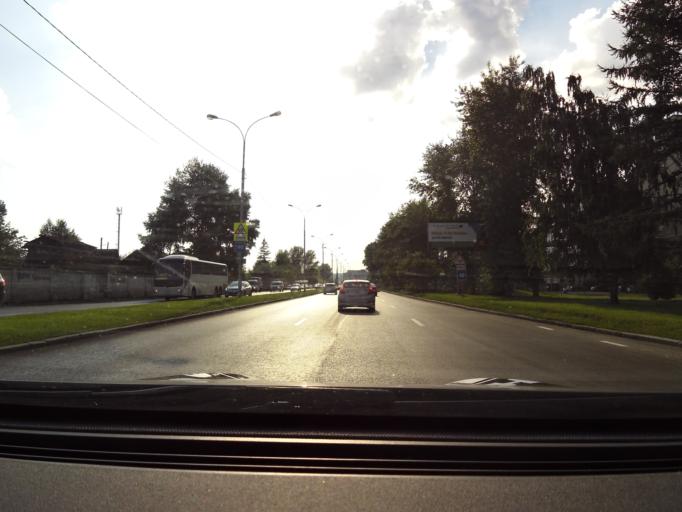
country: RU
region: Sverdlovsk
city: Shirokaya Rechka
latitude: 56.8268
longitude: 60.5377
